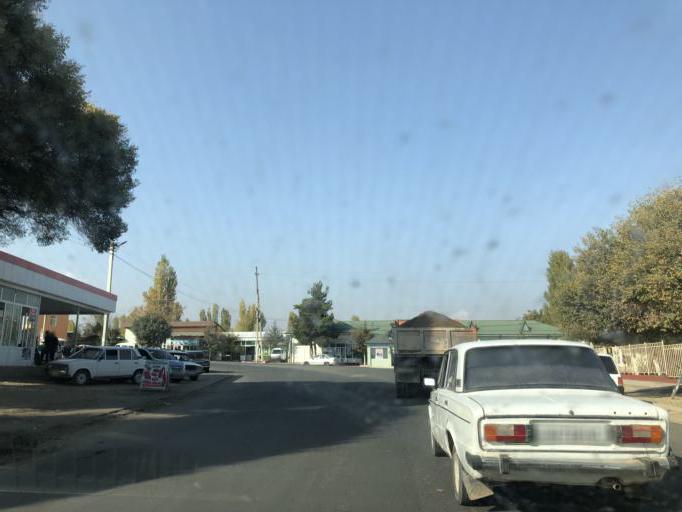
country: UZ
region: Namangan
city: Chust Shahri
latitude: 41.0728
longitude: 71.2044
